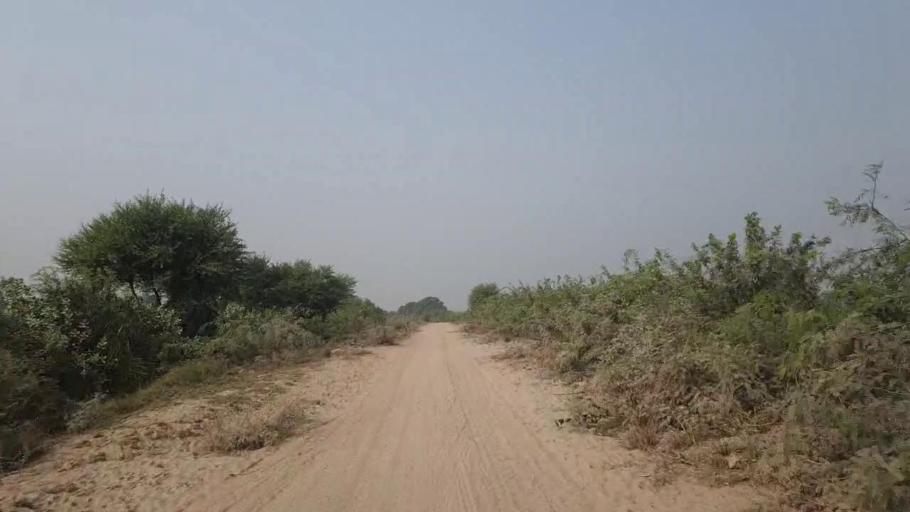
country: PK
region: Sindh
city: Tando Muhammad Khan
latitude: 25.1945
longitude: 68.5765
